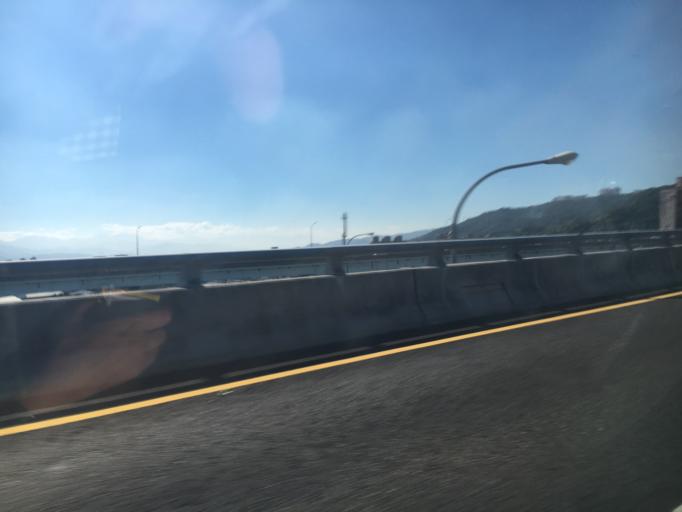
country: TW
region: Taipei
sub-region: Taipei
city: Banqiao
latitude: 25.0695
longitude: 121.4393
